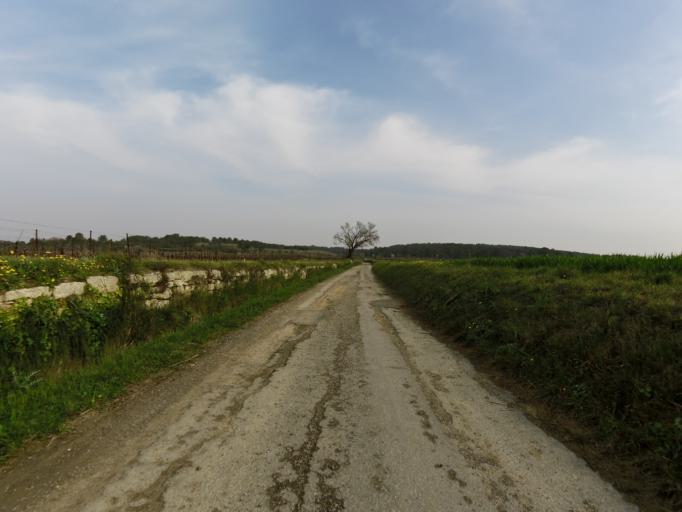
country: FR
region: Languedoc-Roussillon
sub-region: Departement du Gard
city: Aigues-Vives
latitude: 43.7500
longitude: 4.1847
